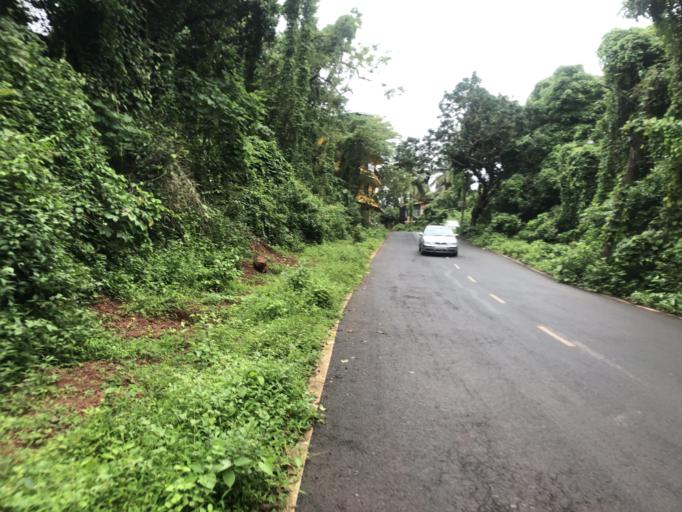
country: IN
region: Goa
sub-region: North Goa
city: Serula
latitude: 15.5411
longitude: 73.8319
